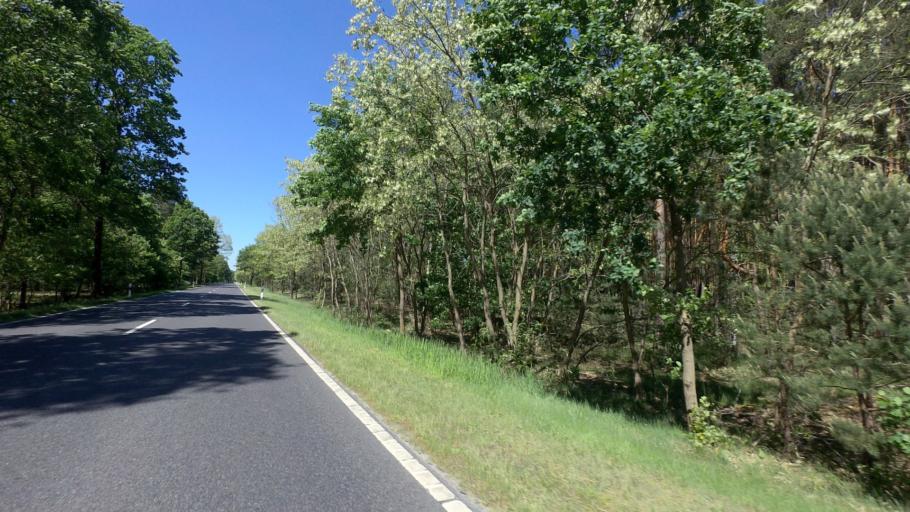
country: DE
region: Brandenburg
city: Lieberose
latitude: 51.9614
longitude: 14.3217
